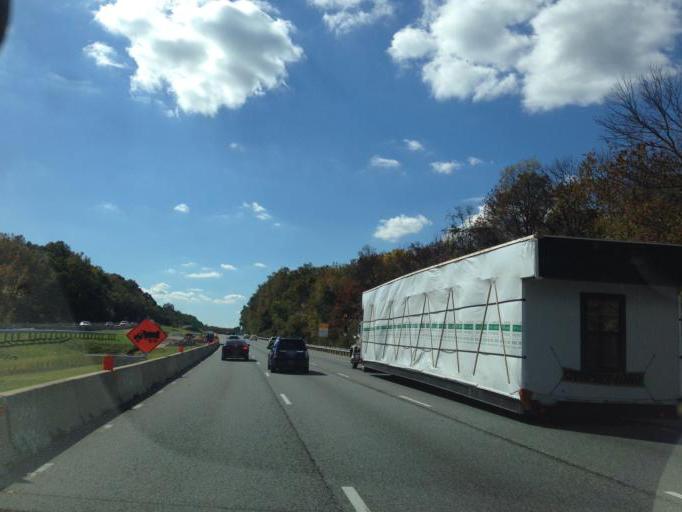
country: US
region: Maryland
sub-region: Howard County
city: Columbia
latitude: 39.2197
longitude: -76.8491
